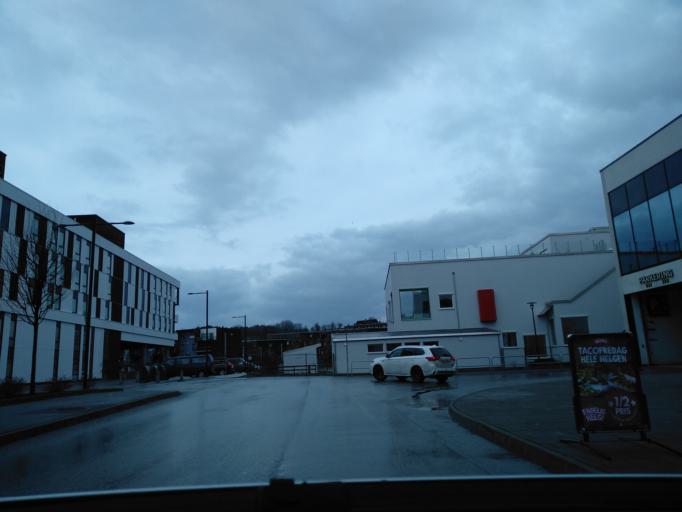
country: NO
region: Rogaland
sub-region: Stavanger
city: Stavanger
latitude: 58.9840
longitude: 5.6900
